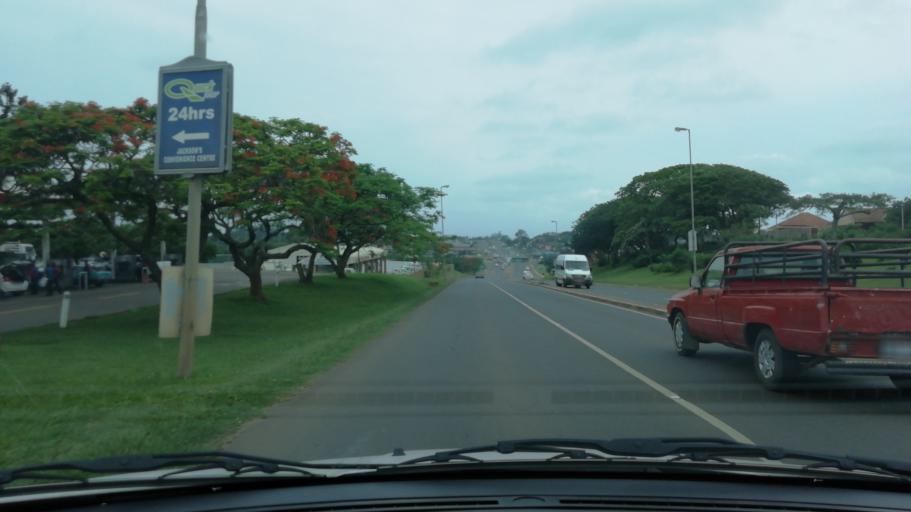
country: ZA
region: KwaZulu-Natal
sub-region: uThungulu District Municipality
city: Empangeni
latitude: -28.7604
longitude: 31.9036
